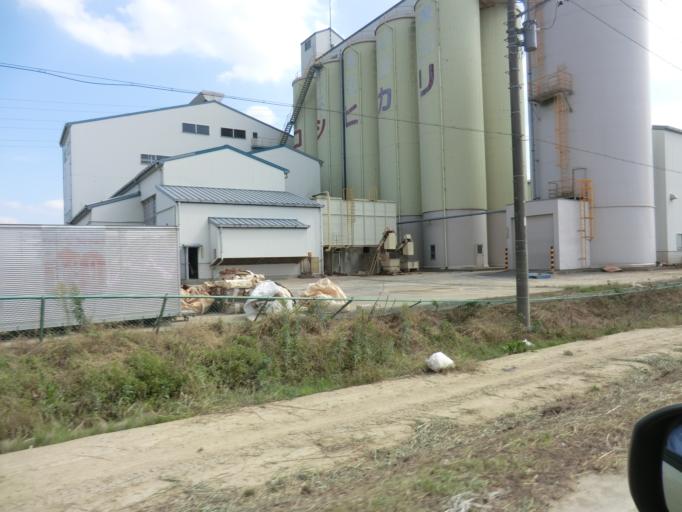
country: JP
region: Ibaraki
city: Mitsukaido
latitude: 36.0629
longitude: 139.9919
